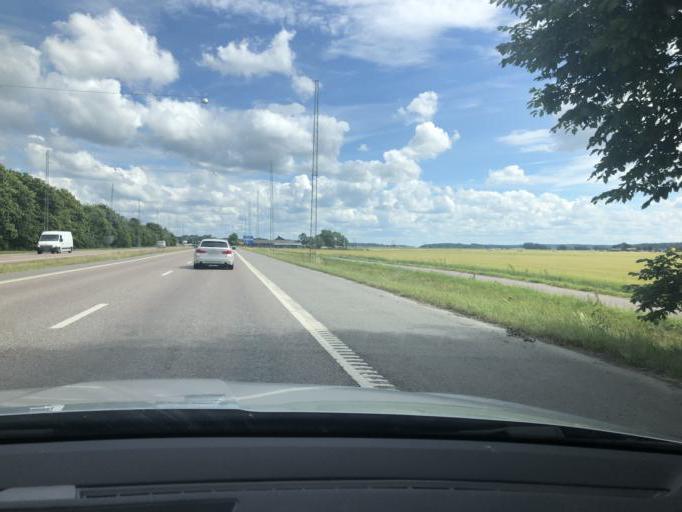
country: SE
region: Uppsala
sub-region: Uppsala Kommun
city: Saevja
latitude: 59.8446
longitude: 17.6821
